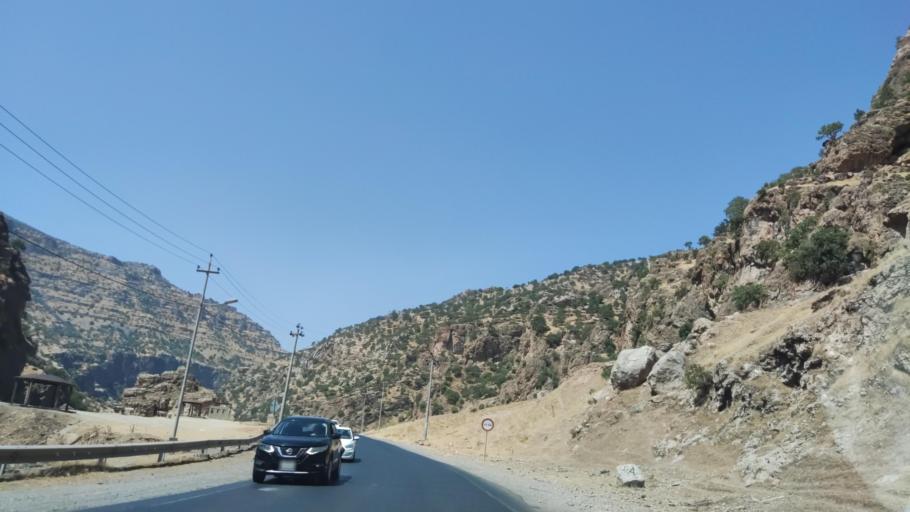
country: IQ
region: Arbil
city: Ruwandiz
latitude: 36.6314
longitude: 44.4791
